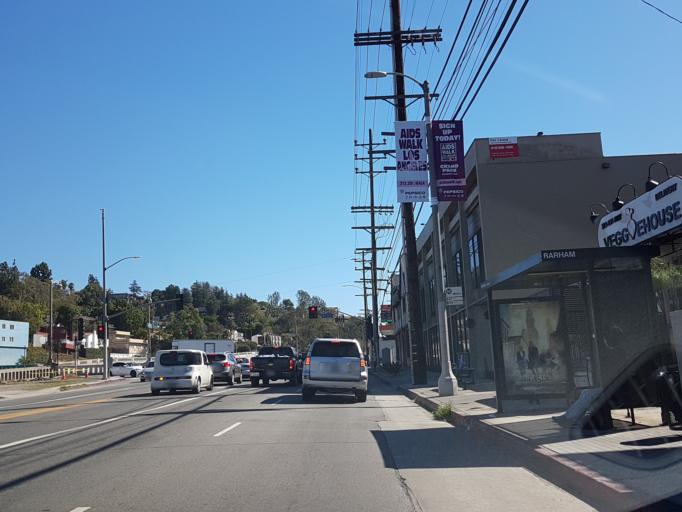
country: US
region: California
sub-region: Los Angeles County
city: Universal City
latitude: 34.1288
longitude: -118.3479
